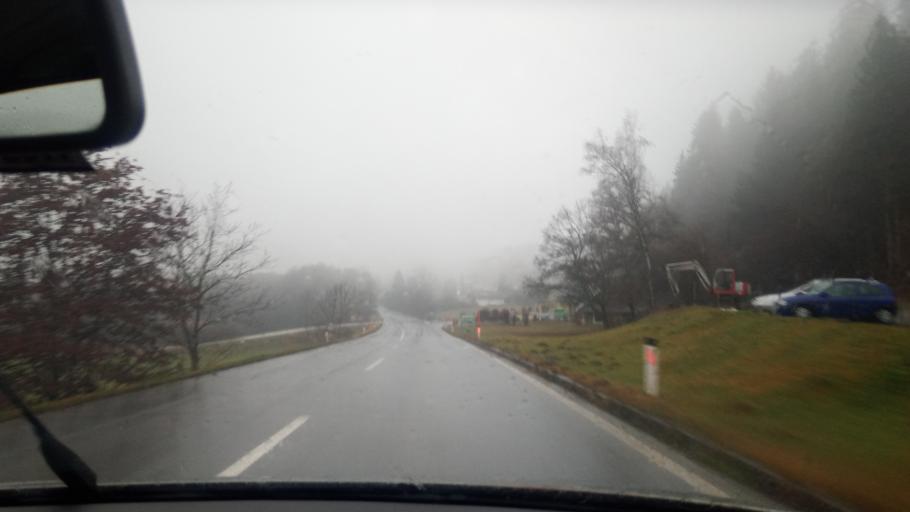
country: AT
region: Carinthia
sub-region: Politischer Bezirk Klagenfurt Land
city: Keutschach am See
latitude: 46.5912
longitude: 14.1957
